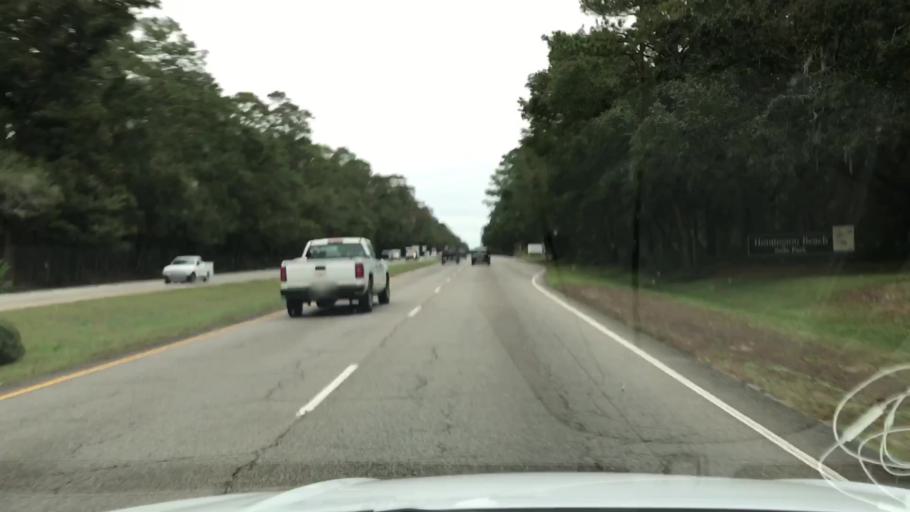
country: US
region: South Carolina
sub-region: Georgetown County
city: Murrells Inlet
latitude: 33.5126
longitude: -79.0740
